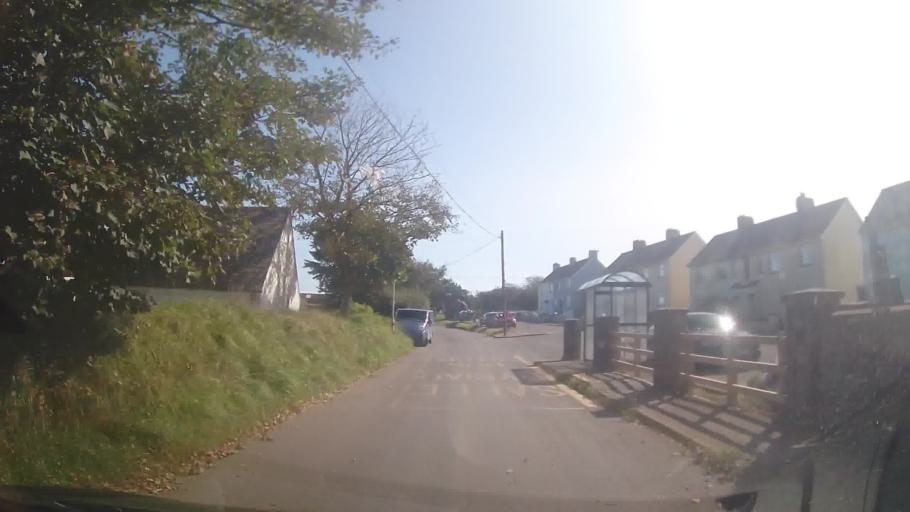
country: GB
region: Wales
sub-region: Pembrokeshire
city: Llanrhian
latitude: 51.9379
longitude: -5.1737
